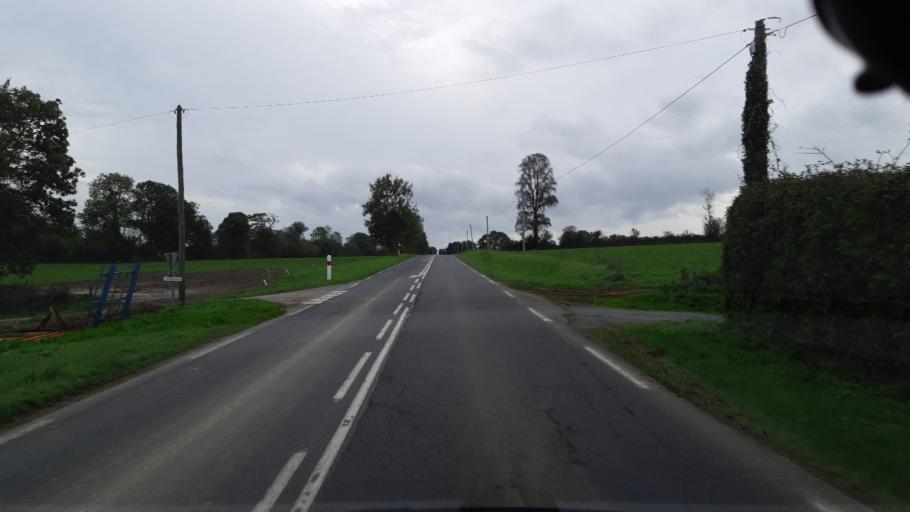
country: FR
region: Lower Normandy
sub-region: Departement de la Manche
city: Gavray
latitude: 48.9381
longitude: -1.3461
